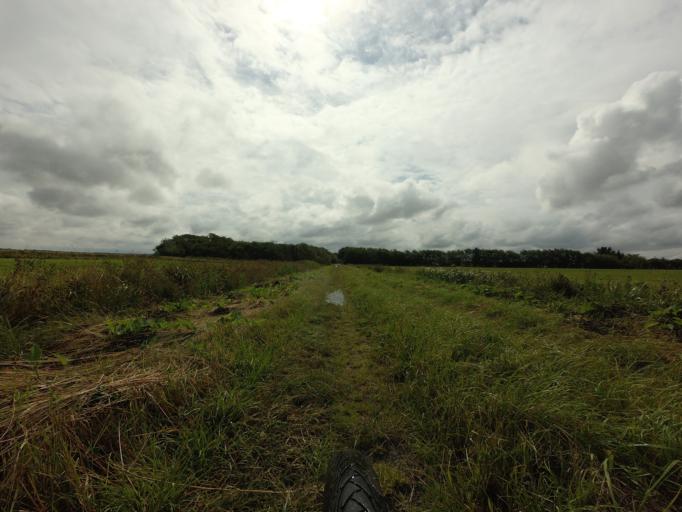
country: DK
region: North Denmark
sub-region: Jammerbugt Kommune
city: Pandrup
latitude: 57.3153
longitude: 9.7435
